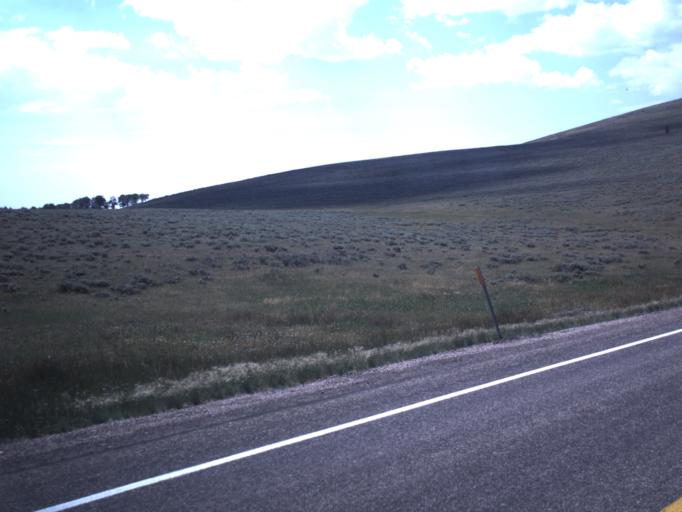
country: US
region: Utah
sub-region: Uintah County
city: Maeser
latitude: 40.7144
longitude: -109.4797
